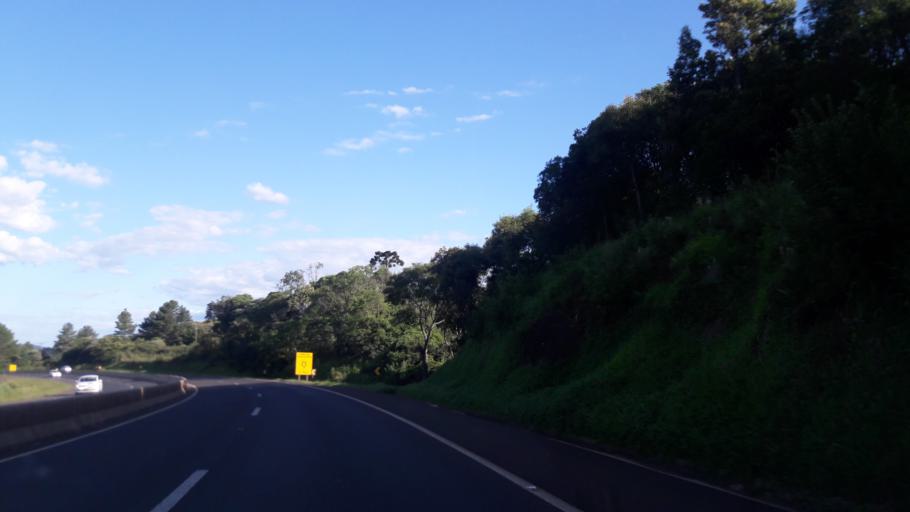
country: BR
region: Parana
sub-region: Guarapuava
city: Guarapuava
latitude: -25.3526
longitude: -51.3748
